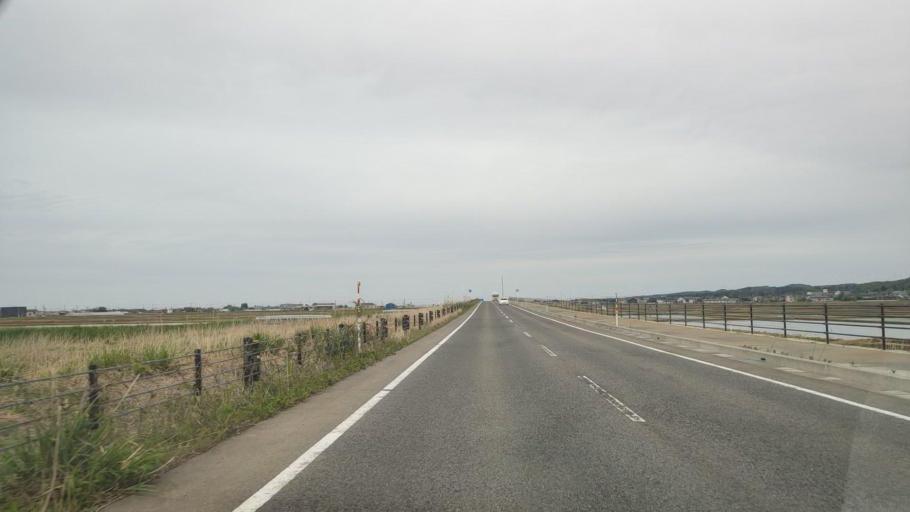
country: JP
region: Niigata
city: Shirone
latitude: 37.7443
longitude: 139.0826
